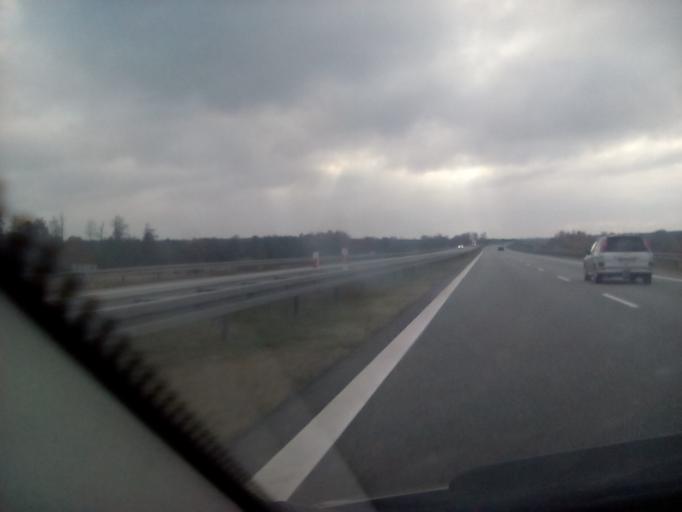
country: PL
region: Masovian Voivodeship
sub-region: Powiat bialobrzeski
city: Bialobrzegi
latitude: 51.6612
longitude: 20.9606
